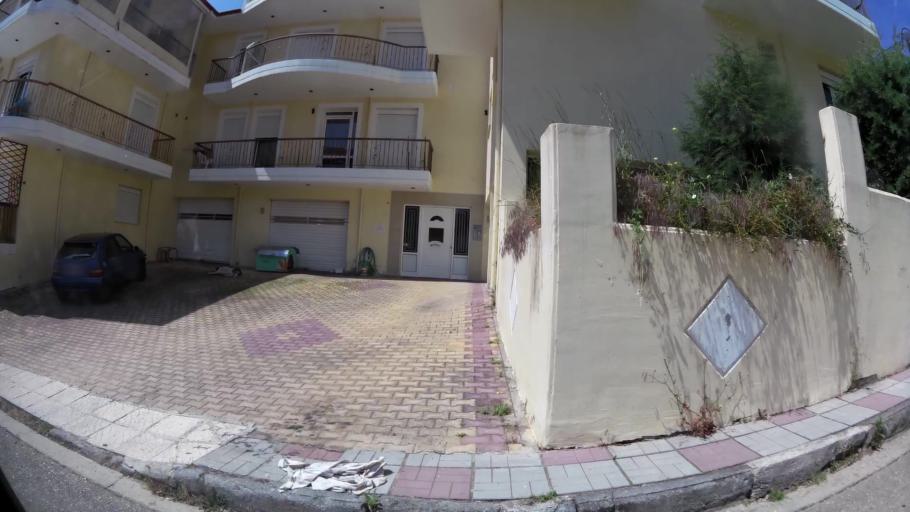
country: GR
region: West Macedonia
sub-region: Nomos Kozanis
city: Kozani
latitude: 40.3020
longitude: 21.7782
